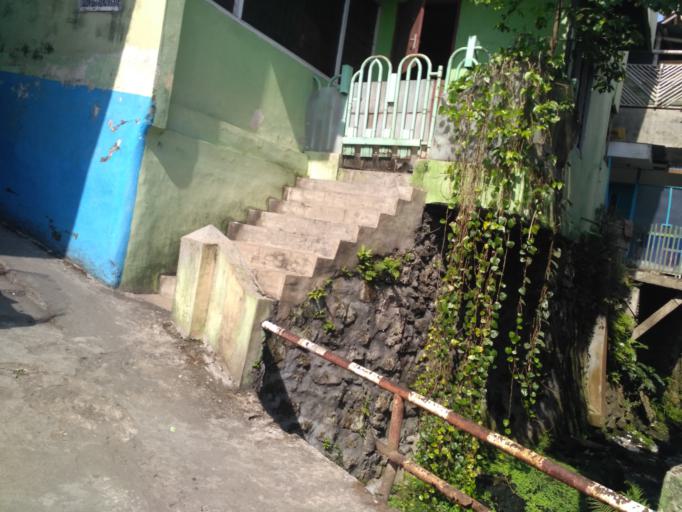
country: ID
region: East Java
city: Malang
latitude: -7.9372
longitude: 112.6052
